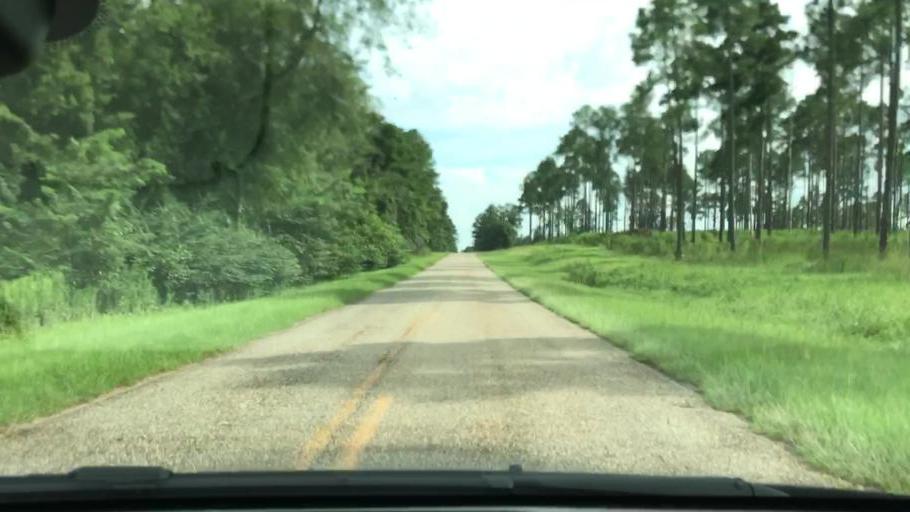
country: US
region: Georgia
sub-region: Clay County
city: Fort Gaines
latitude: 31.5157
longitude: -84.9540
